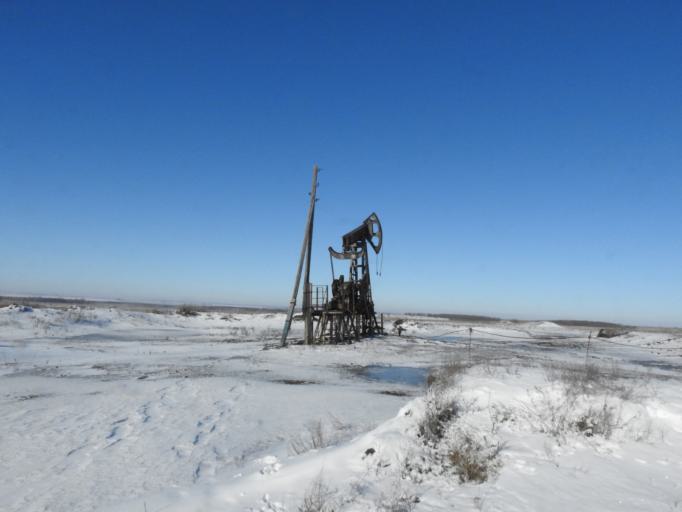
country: RU
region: Saratov
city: Lysyye Gory
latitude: 51.4569
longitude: 44.9634
